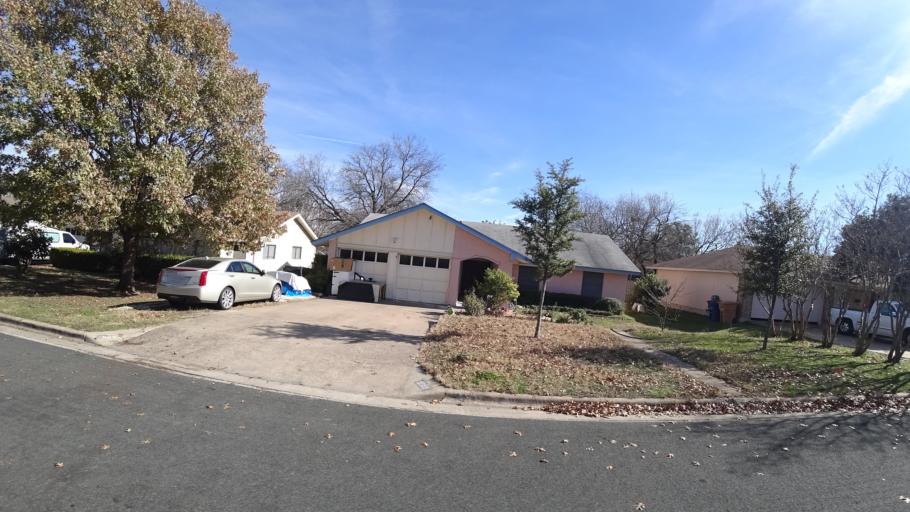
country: US
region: Texas
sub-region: Travis County
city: Wells Branch
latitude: 30.3720
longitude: -97.7080
